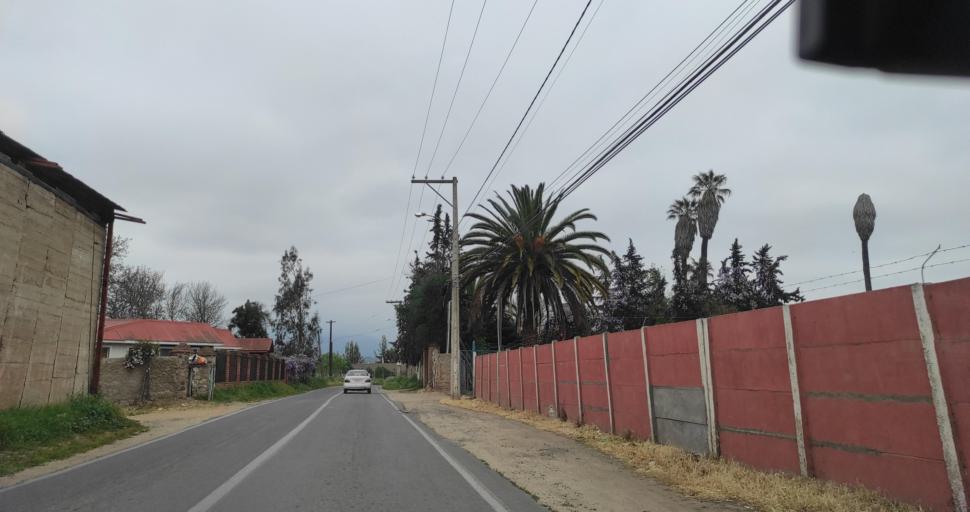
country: CL
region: Valparaiso
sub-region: Provincia de Marga Marga
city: Limache
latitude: -33.0047
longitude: -71.2392
